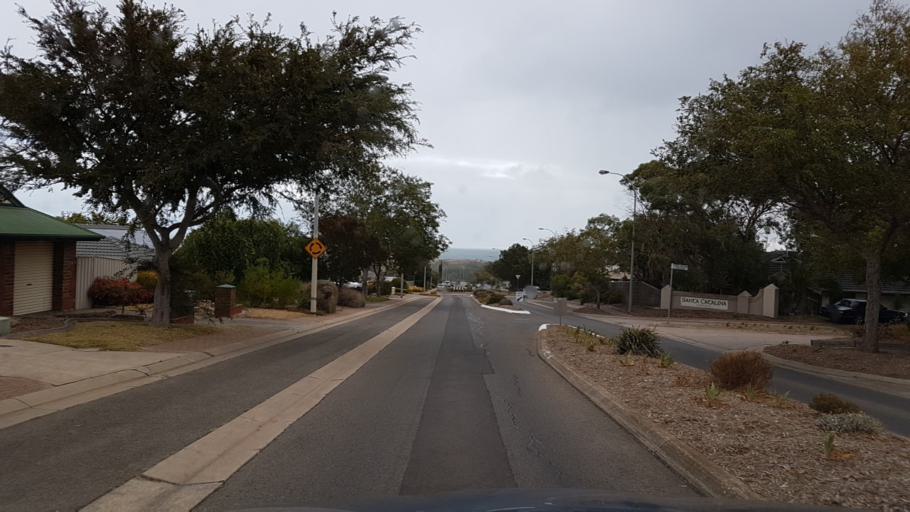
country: AU
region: South Australia
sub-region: Onkaparinga
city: Moana
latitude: -35.2015
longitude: 138.4842
